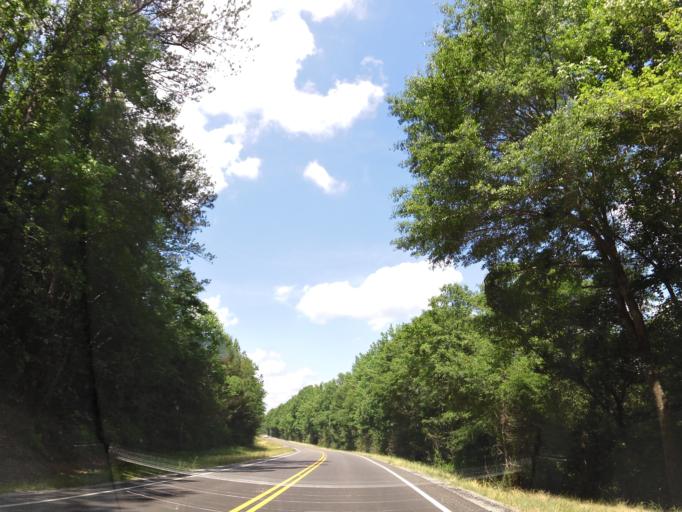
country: US
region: Alabama
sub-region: Marion County
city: Guin
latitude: 33.9549
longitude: -87.9633
